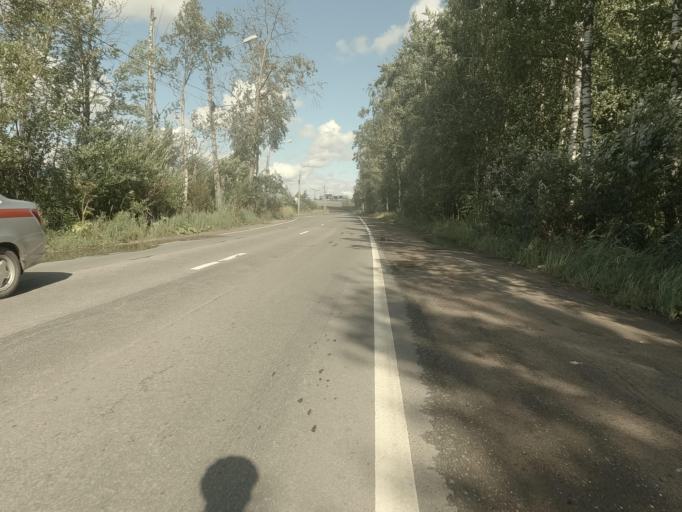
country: RU
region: St.-Petersburg
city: Krasnogvargeisky
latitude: 59.9737
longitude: 30.5319
